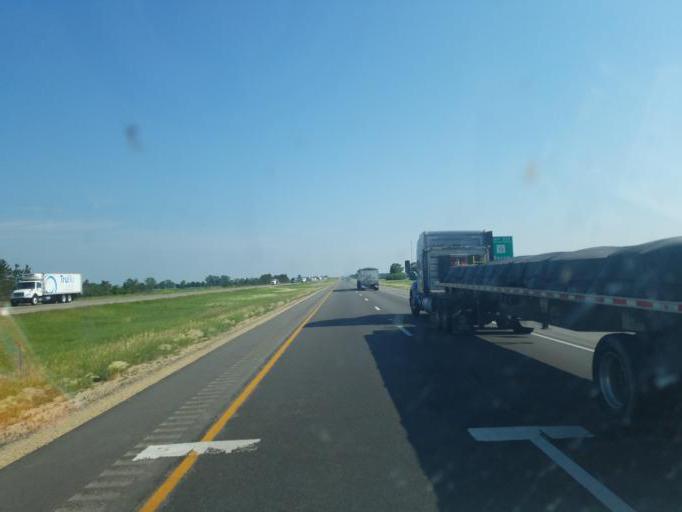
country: US
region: Illinois
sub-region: Ogle County
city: Davis Junction
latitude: 42.0868
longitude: -89.0225
